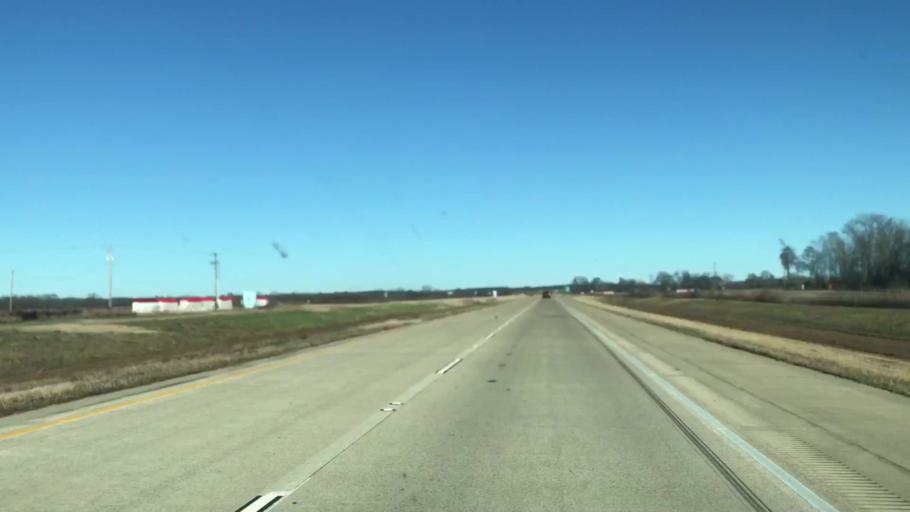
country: US
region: Louisiana
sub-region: Caddo Parish
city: Oil City
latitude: 32.7509
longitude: -93.8818
